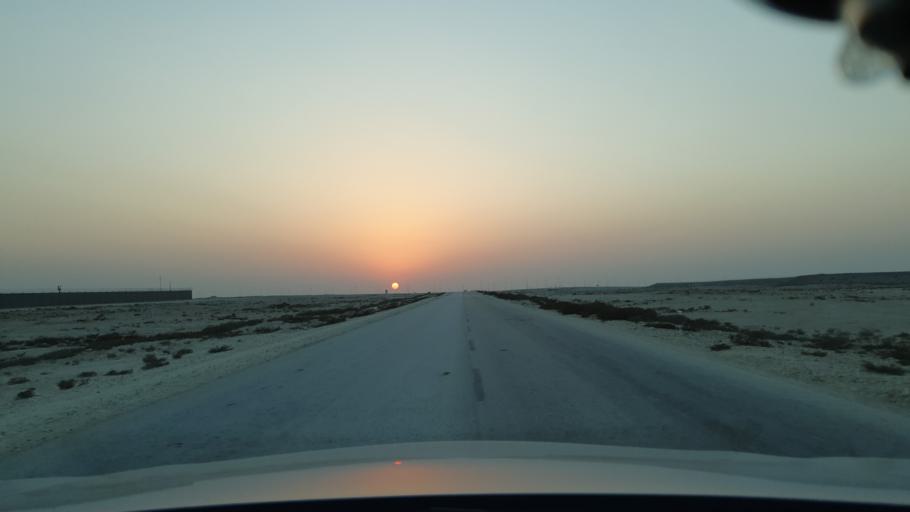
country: BH
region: Central Governorate
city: Dar Kulayb
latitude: 25.9558
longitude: 50.6043
